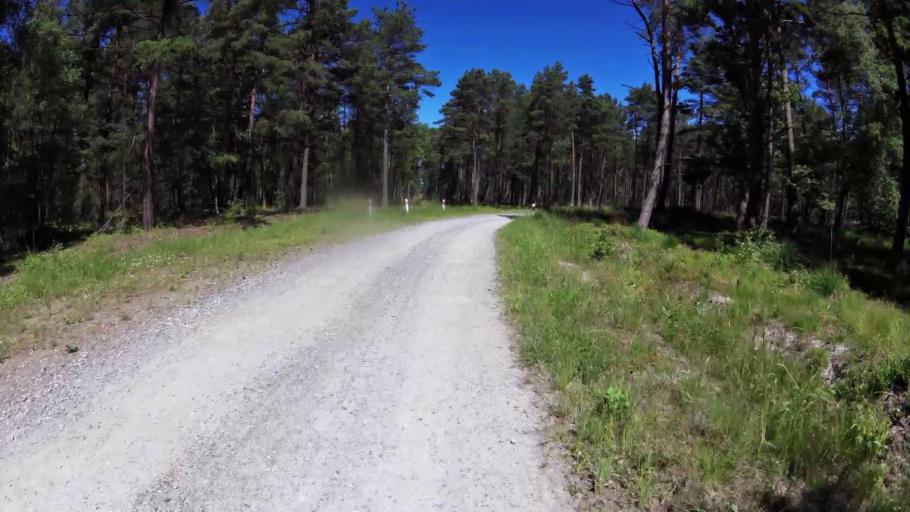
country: PL
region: West Pomeranian Voivodeship
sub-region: Powiat gryficki
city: Trzebiatow
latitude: 54.1020
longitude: 15.1708
